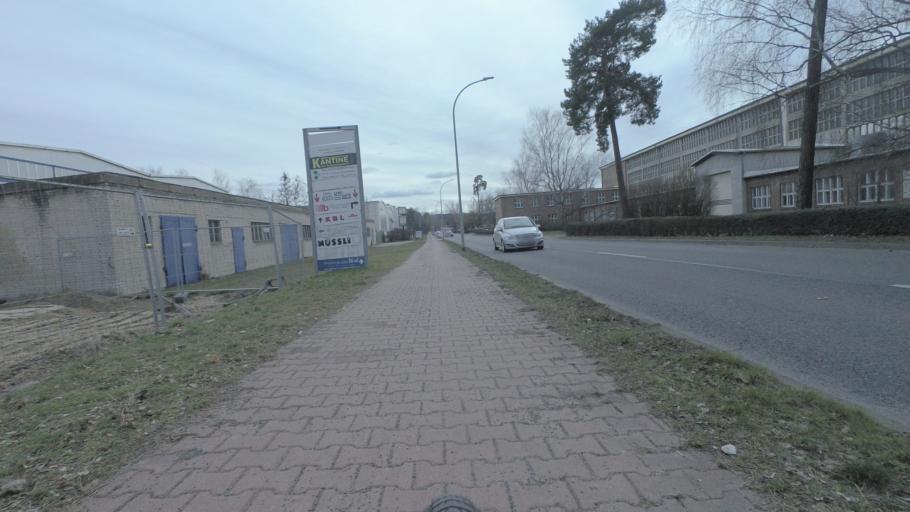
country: DE
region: Brandenburg
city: Ludwigsfelde
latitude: 52.3244
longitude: 13.2641
